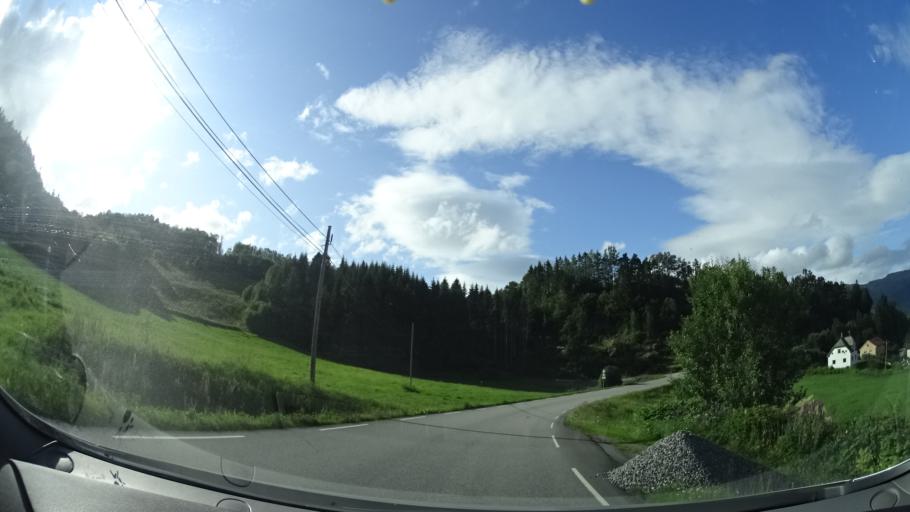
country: NO
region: More og Romsdal
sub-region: Aure
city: Aure
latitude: 63.1351
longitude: 8.4949
